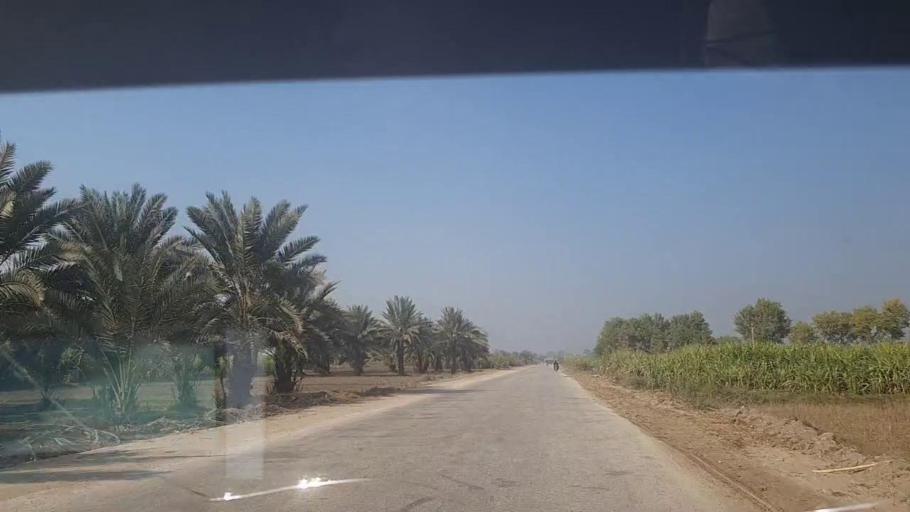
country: PK
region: Sindh
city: Kot Diji
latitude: 27.4215
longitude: 68.6601
